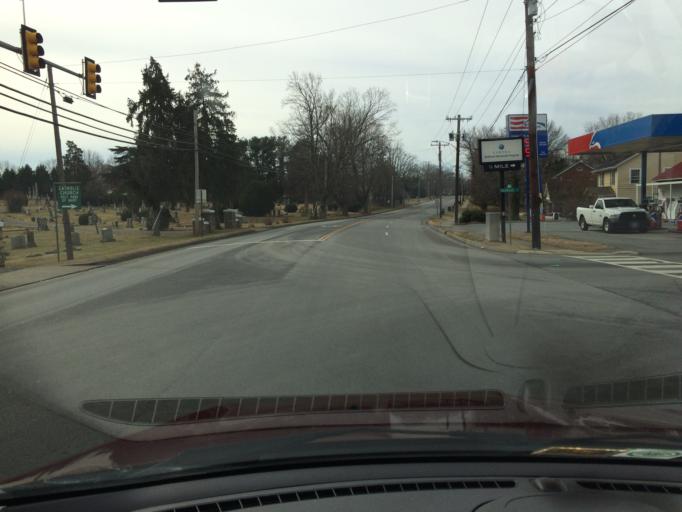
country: US
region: Virginia
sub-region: City of Bedford
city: Bedford
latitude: 37.3432
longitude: -79.5113
